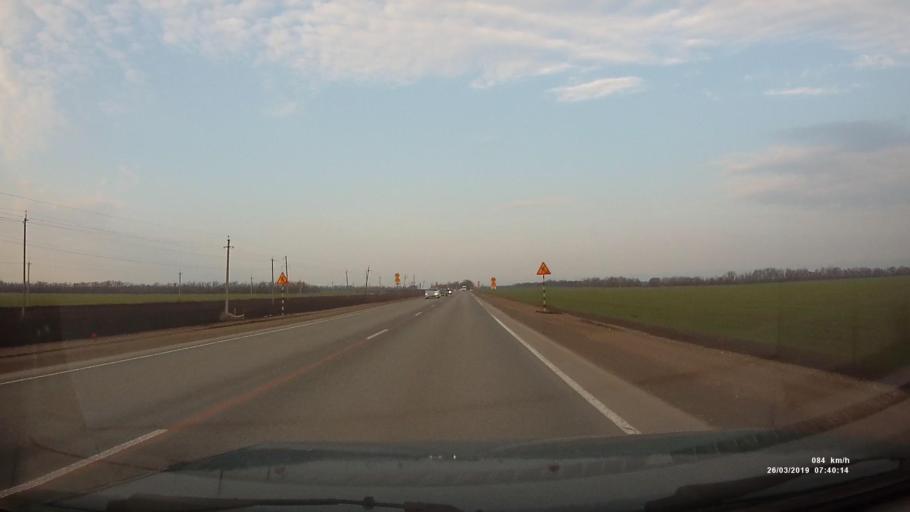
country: RU
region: Rostov
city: Novobessergenovka
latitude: 47.1950
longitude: 38.6529
